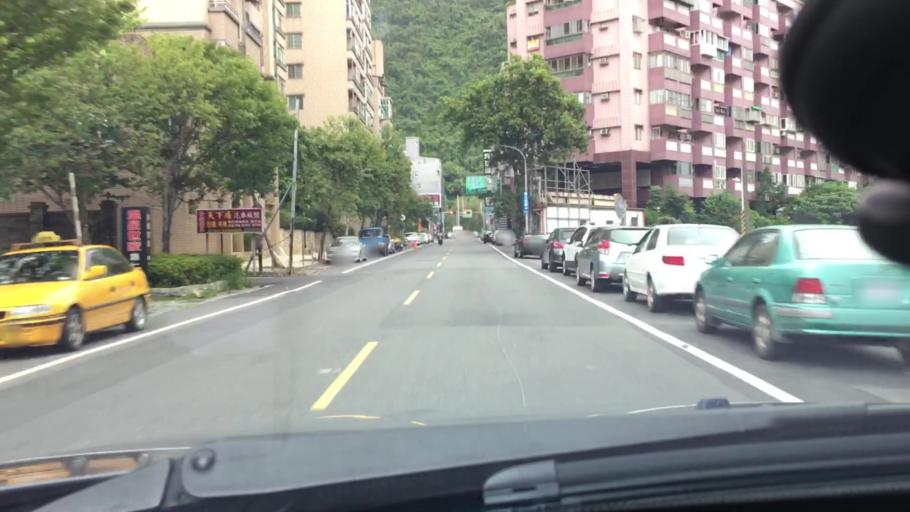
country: TW
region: Taiwan
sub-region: Yilan
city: Yilan
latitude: 24.8245
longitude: 121.7643
